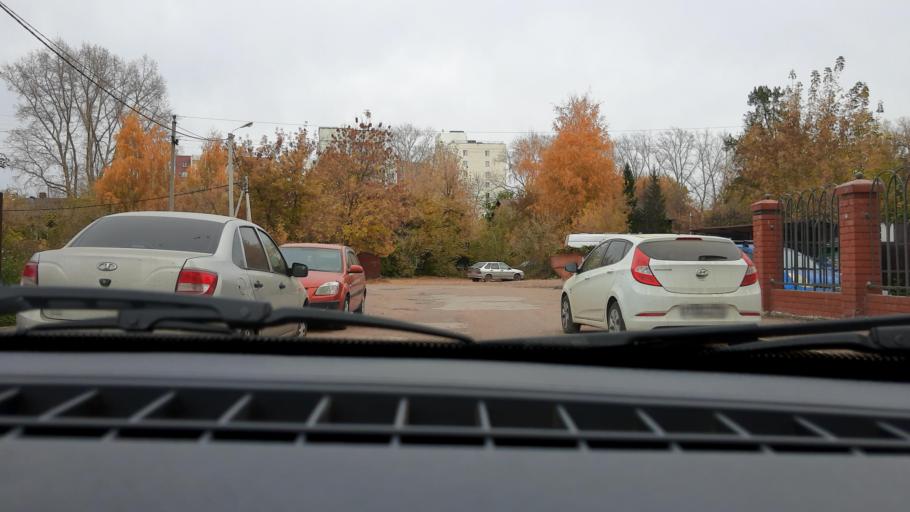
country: RU
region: Bashkortostan
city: Mikhaylovka
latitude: 54.7817
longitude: 55.8834
